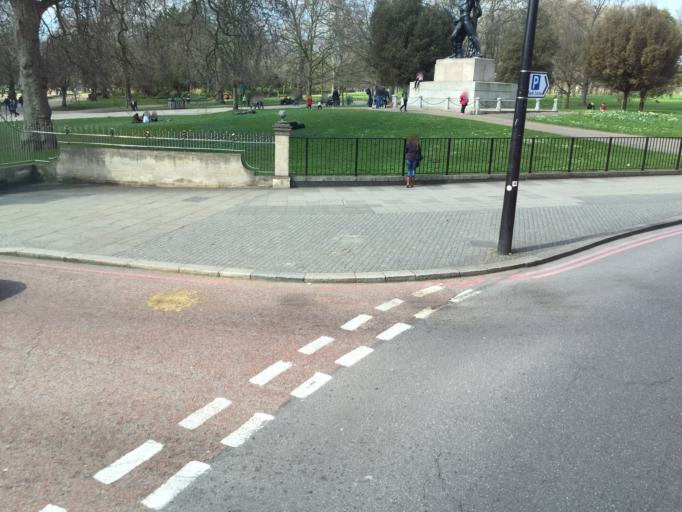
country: GB
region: England
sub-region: Greater London
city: Chelsea
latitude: 51.5042
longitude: -0.1520
